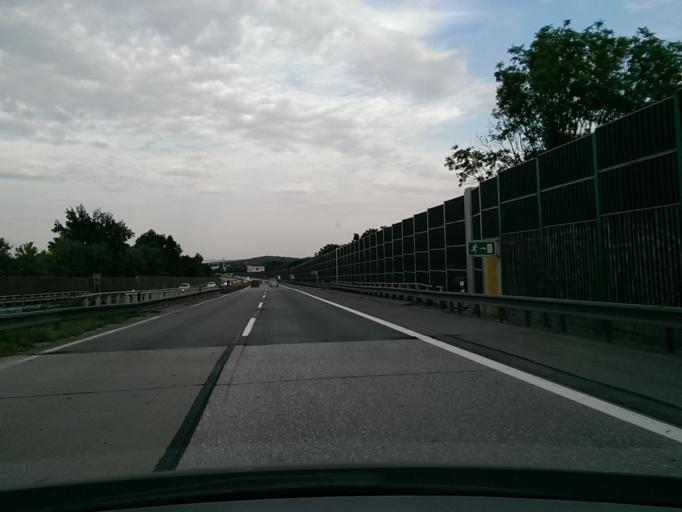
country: CZ
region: South Moravian
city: Troubsko
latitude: 49.1792
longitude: 16.4886
